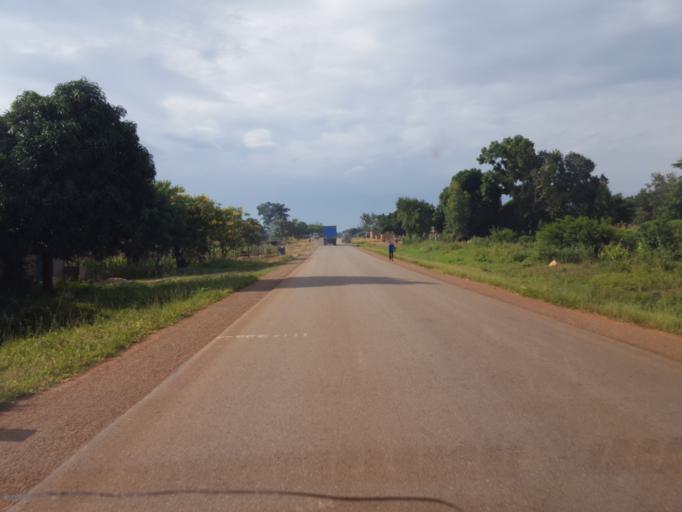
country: UG
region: Central Region
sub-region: Kyankwanzi District
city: Kyankwanzi
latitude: 1.2245
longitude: 31.5477
